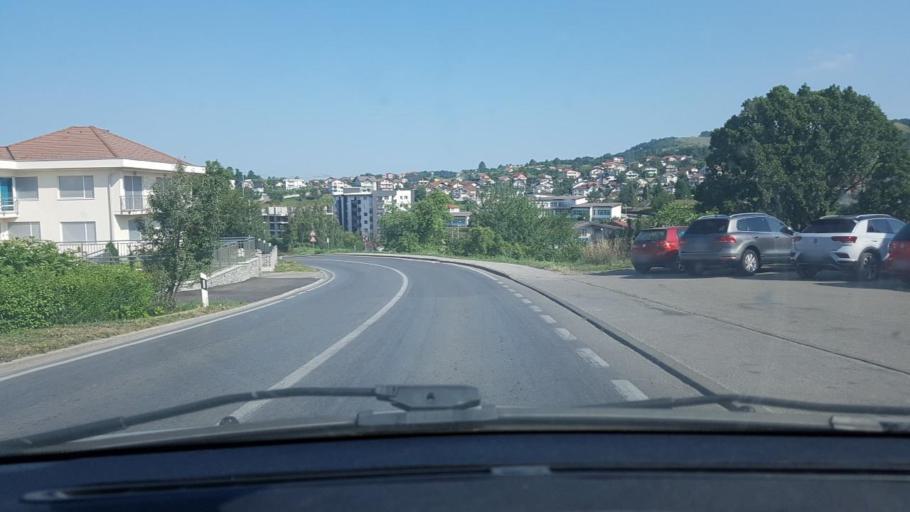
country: BA
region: Federation of Bosnia and Herzegovina
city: Cazin
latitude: 44.9644
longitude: 15.9264
